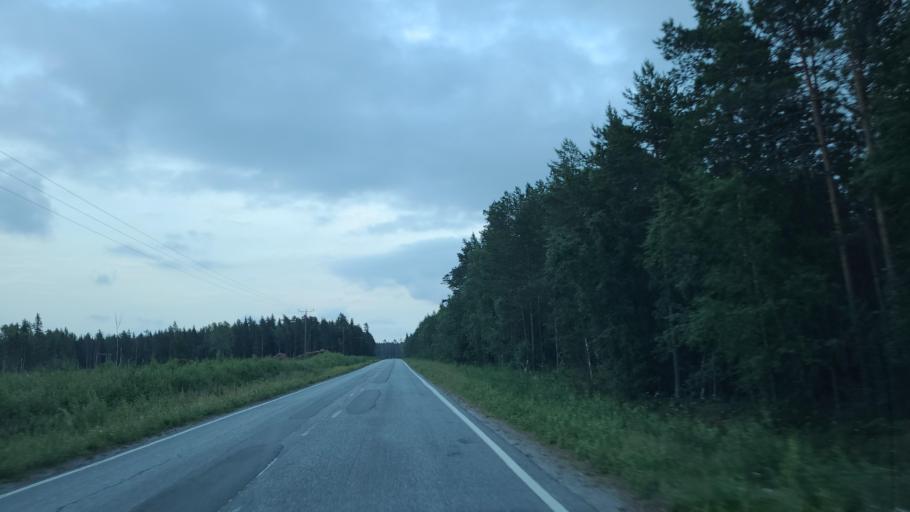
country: FI
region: Ostrobothnia
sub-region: Vaasa
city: Replot
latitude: 63.2075
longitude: 21.2607
